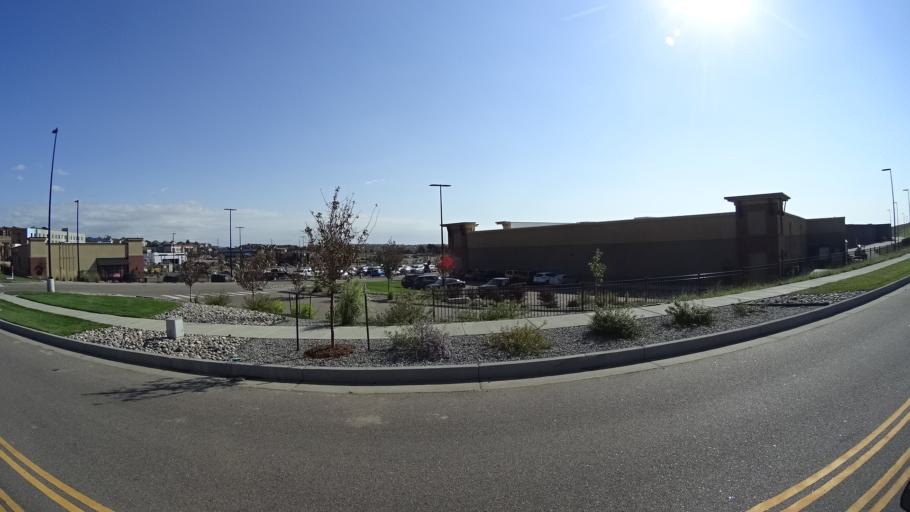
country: US
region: Colorado
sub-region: El Paso County
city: Cimarron Hills
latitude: 38.8932
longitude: -104.7240
